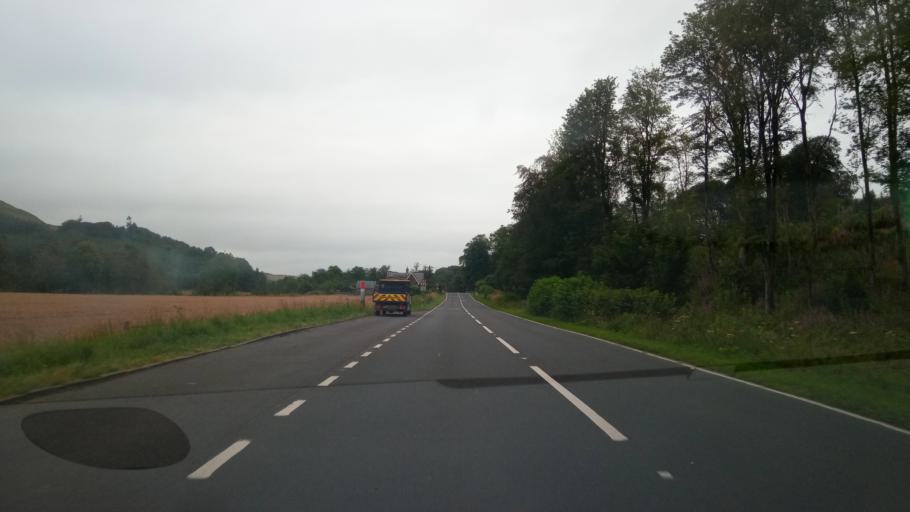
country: GB
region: Scotland
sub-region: The Scottish Borders
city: Hawick
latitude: 55.3975
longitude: -2.8430
